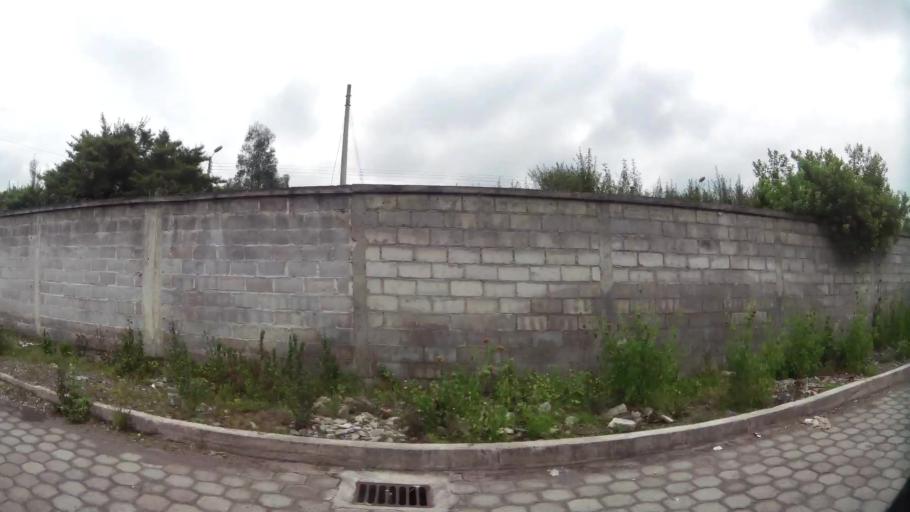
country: EC
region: Pichincha
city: Sangolqui
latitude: -0.3455
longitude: -78.4692
